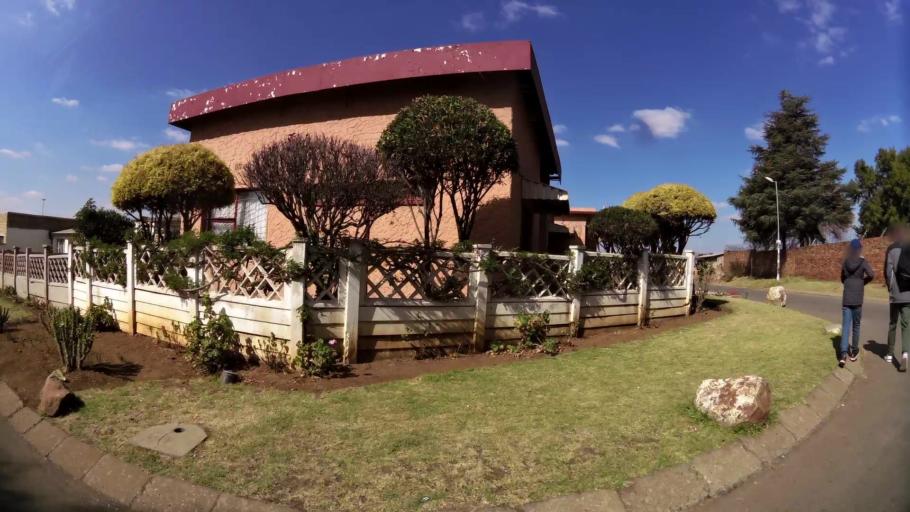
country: ZA
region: Gauteng
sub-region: City of Johannesburg Metropolitan Municipality
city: Soweto
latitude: -26.2476
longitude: 27.8846
